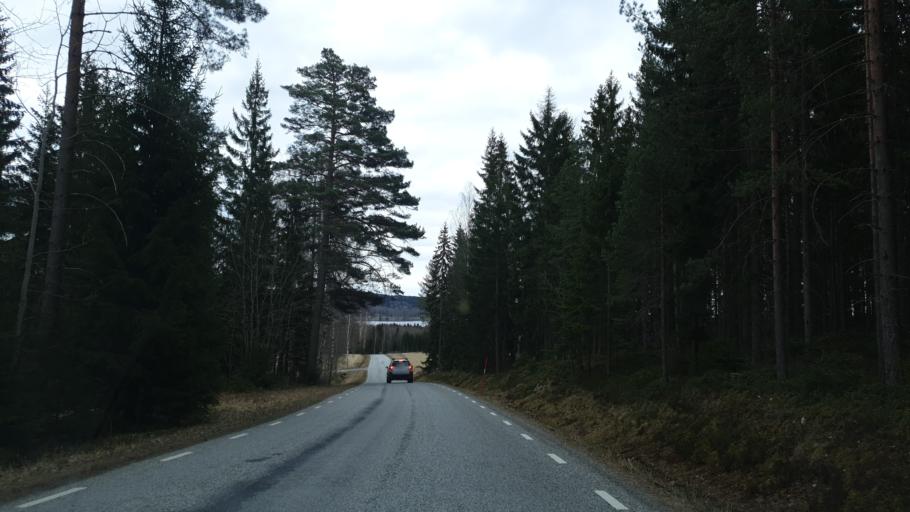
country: SE
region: OErebro
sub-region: Nora Kommun
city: As
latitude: 59.6142
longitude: 14.9800
